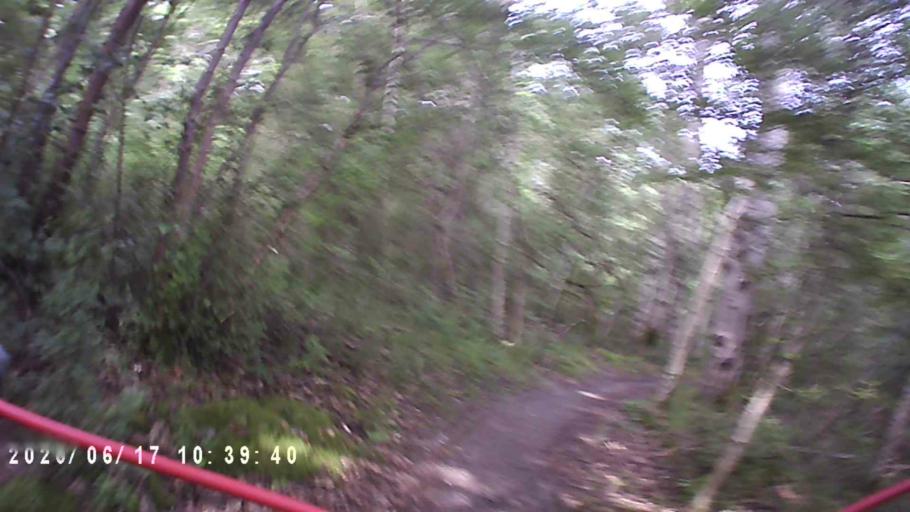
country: NL
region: Friesland
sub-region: Gemeente Dongeradeel
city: Anjum
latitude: 53.4024
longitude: 6.2319
